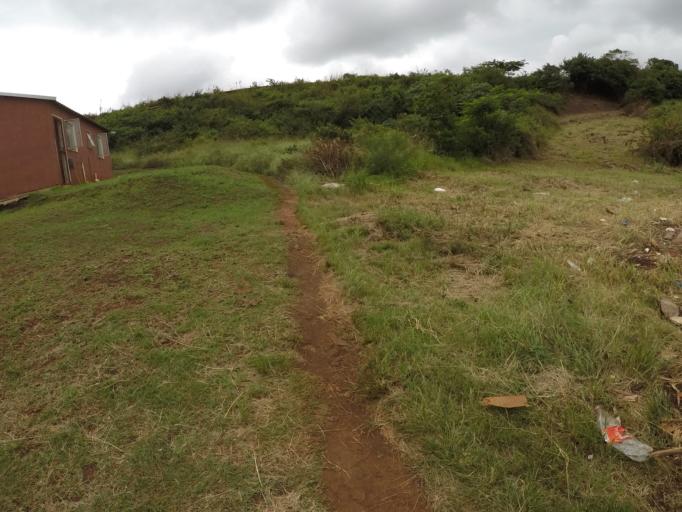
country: ZA
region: KwaZulu-Natal
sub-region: uThungulu District Municipality
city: Empangeni
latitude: -28.7595
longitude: 31.8749
